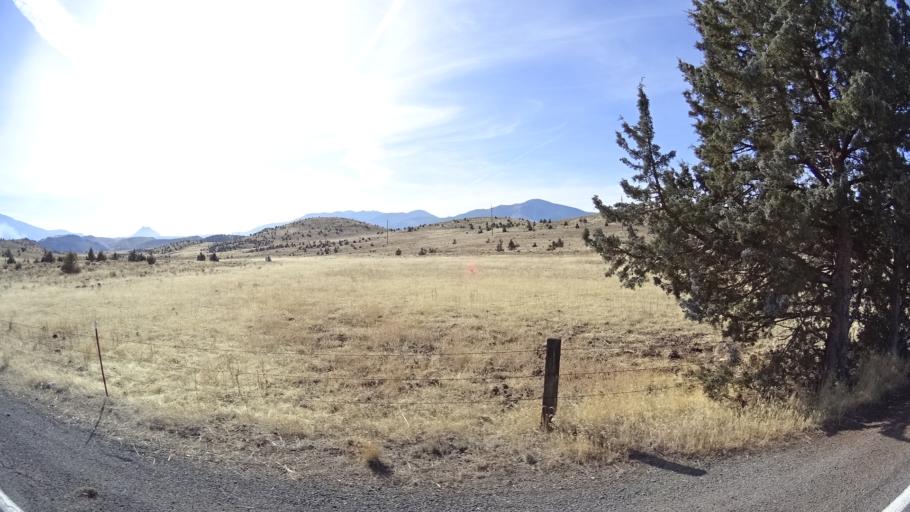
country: US
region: California
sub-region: Siskiyou County
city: Weed
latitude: 41.5540
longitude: -122.4790
